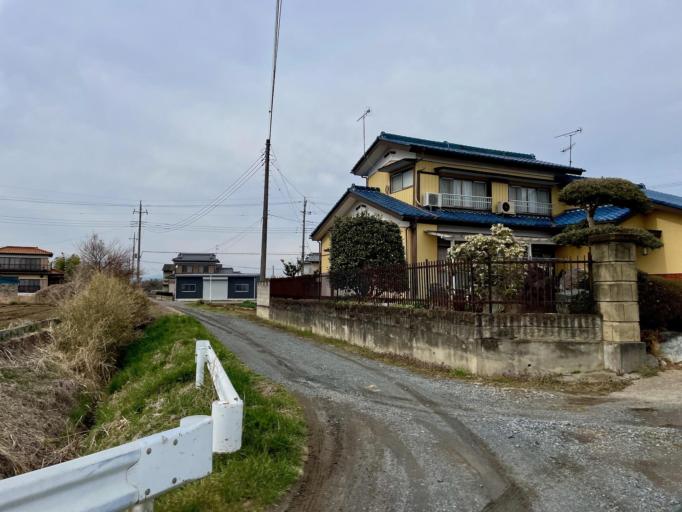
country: JP
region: Saitama
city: Kodamacho-kodamaminami
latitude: 36.2052
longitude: 139.1201
